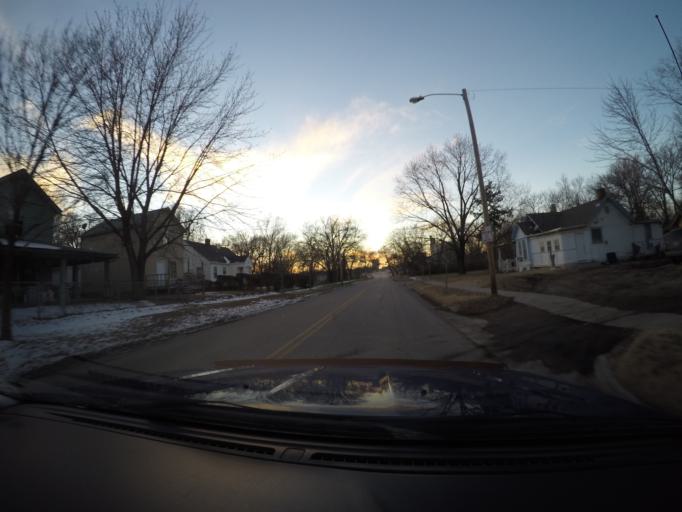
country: US
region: Kansas
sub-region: Shawnee County
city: Topeka
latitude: 39.0443
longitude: -95.6623
